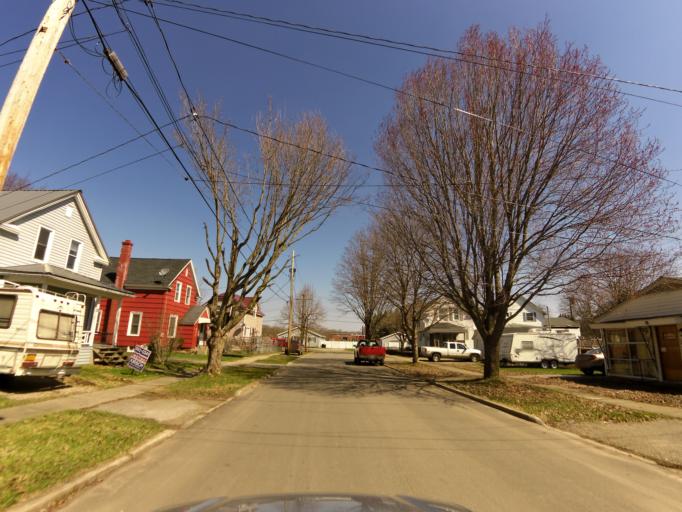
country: US
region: New York
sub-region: Cattaraugus County
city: Franklinville
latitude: 42.3389
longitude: -78.4587
